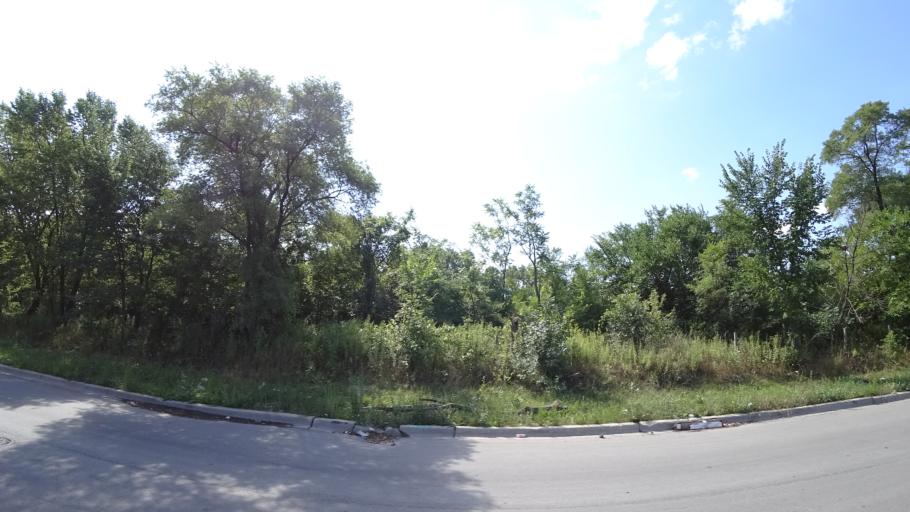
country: US
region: Illinois
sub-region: Cook County
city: Cicero
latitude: 41.8689
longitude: -87.7410
